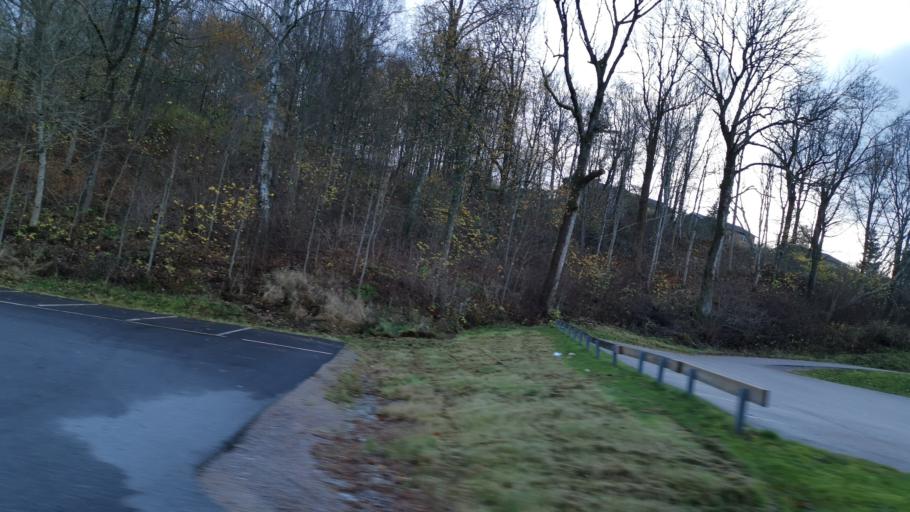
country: SE
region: Vaestra Goetaland
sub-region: Munkedals Kommun
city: Munkedal
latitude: 58.4676
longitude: 11.6691
